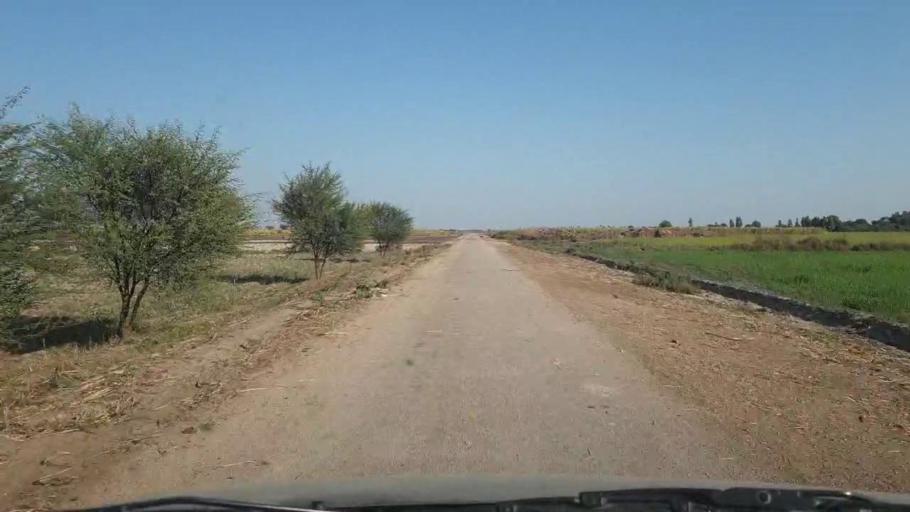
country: PK
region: Sindh
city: Samaro
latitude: 25.3484
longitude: 69.3203
